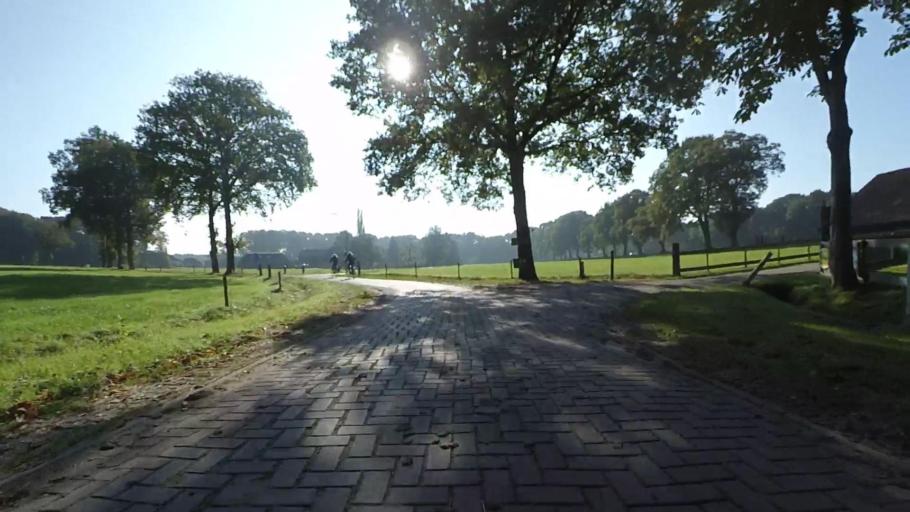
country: NL
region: Gelderland
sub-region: Gemeente Nijkerk
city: Nijkerk
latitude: 52.2284
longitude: 5.5376
